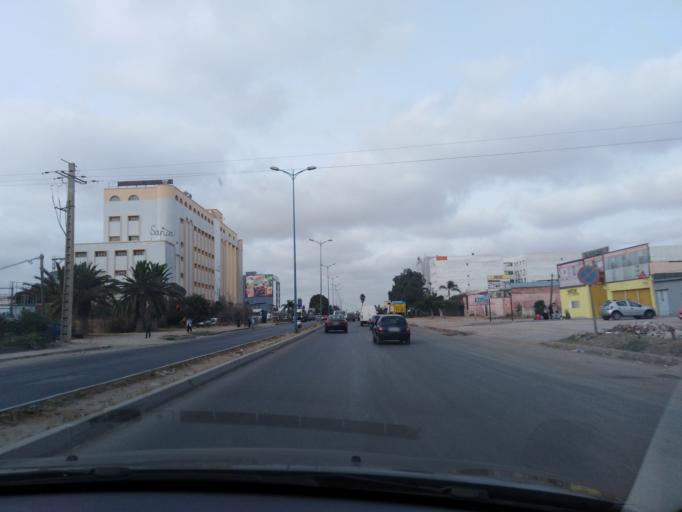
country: MA
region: Grand Casablanca
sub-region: Nouaceur
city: Bouskoura
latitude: 33.5268
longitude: -7.6815
